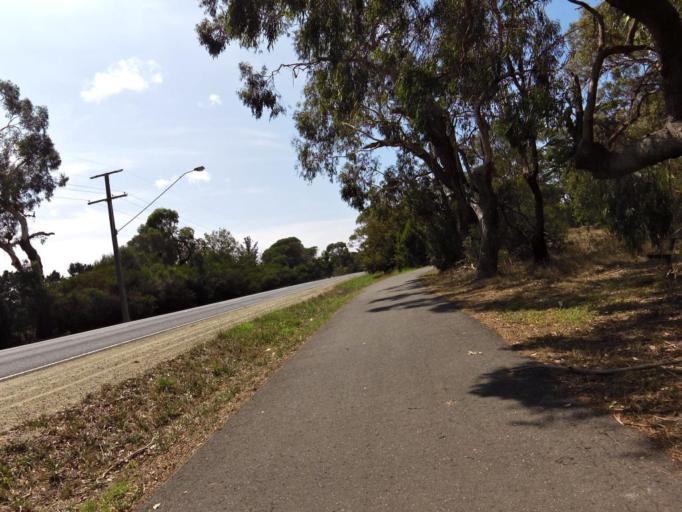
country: AU
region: Victoria
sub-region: Mornington Peninsula
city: Crib Point
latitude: -38.3350
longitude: 145.1791
